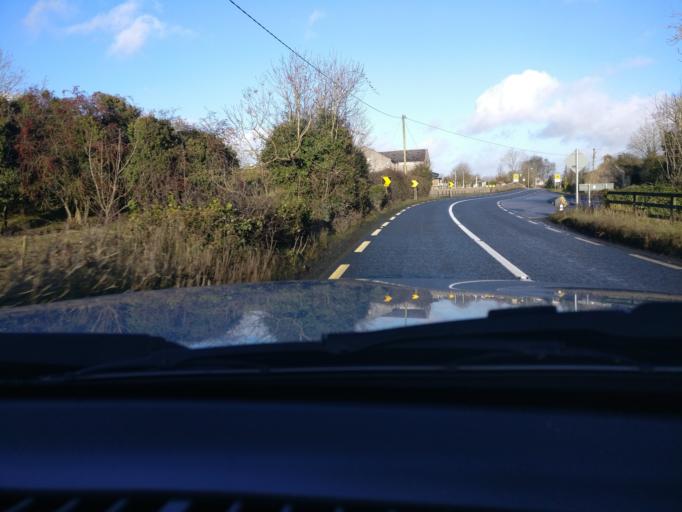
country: IE
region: Leinster
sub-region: An Iarmhi
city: Rathwire
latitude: 53.5665
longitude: -7.1931
